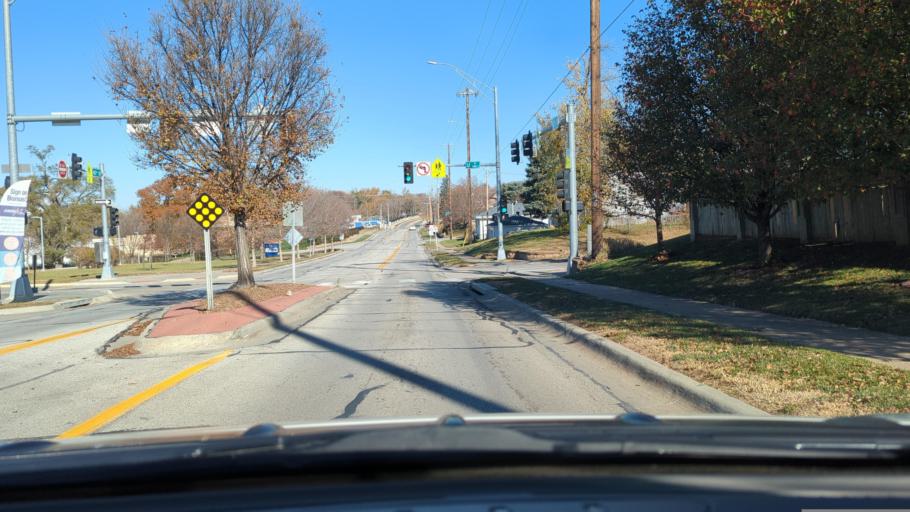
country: US
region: Nebraska
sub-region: Sarpy County
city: La Vista
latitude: 41.2015
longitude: -95.9770
